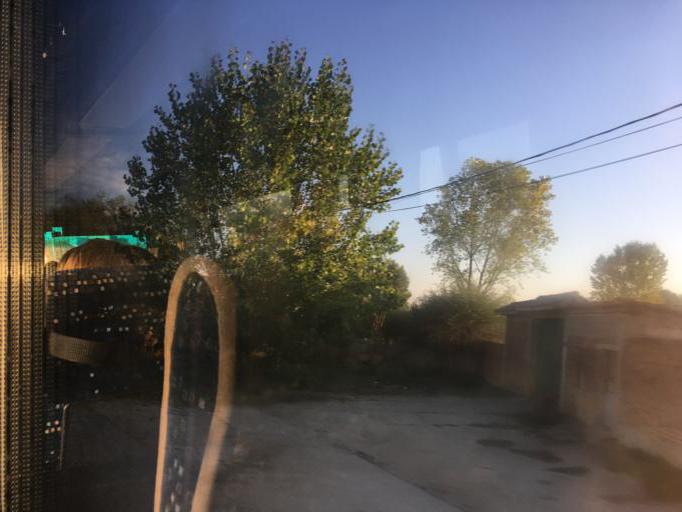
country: XK
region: Pristina
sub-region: Komuna e Drenasit
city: Glogovac
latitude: 42.5901
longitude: 20.8932
